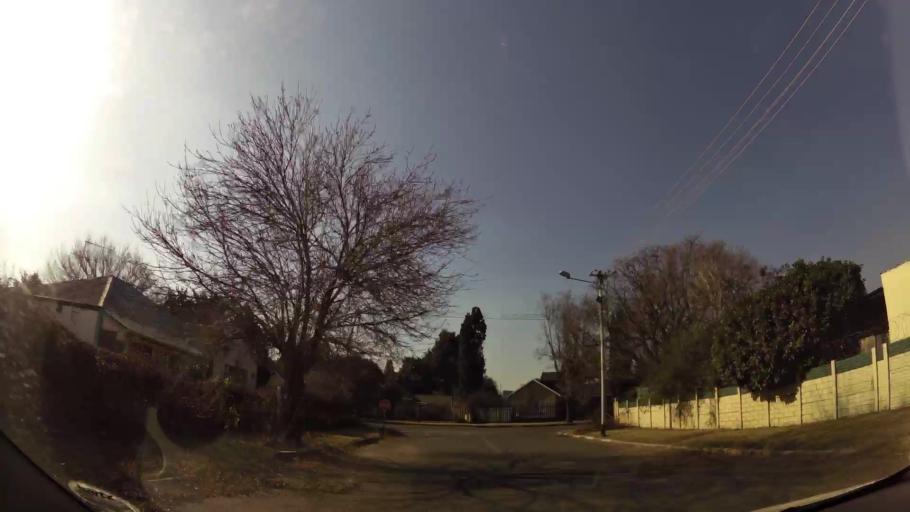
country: ZA
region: Gauteng
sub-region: West Rand District Municipality
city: Randfontein
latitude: -26.1680
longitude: 27.7088
